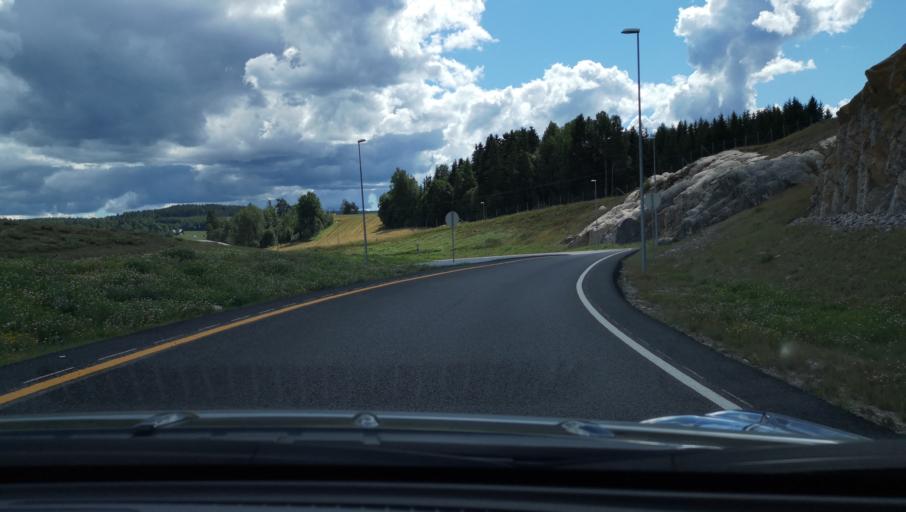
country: NO
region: Ostfold
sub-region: Hobol
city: Elvestad
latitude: 59.6291
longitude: 10.9525
